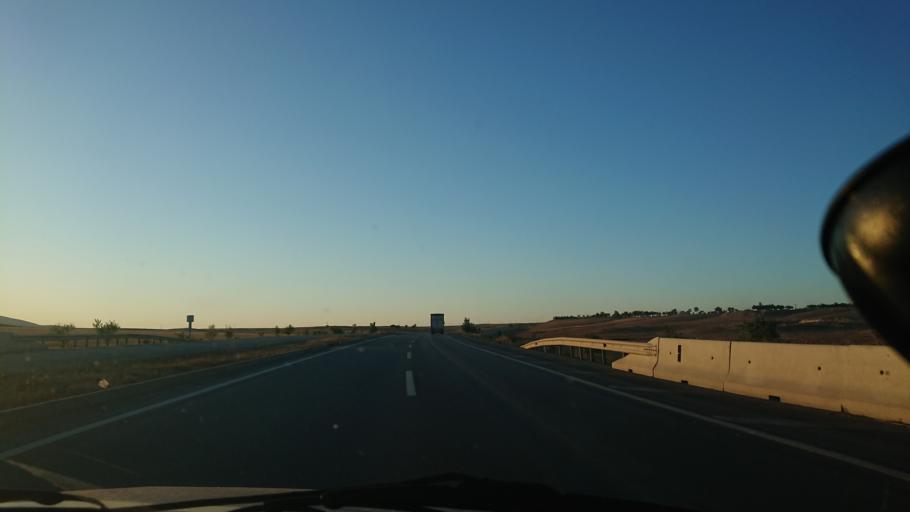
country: TR
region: Eskisehir
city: Mahmudiye
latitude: 39.4969
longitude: 30.9718
